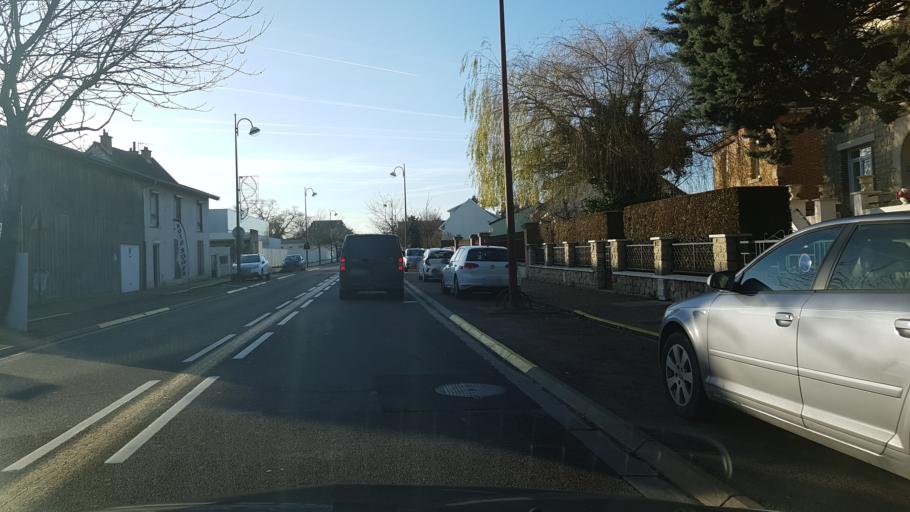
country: FR
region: Champagne-Ardenne
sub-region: Departement de la Marne
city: Vitry-le-Francois
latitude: 48.7295
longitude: 4.5959
